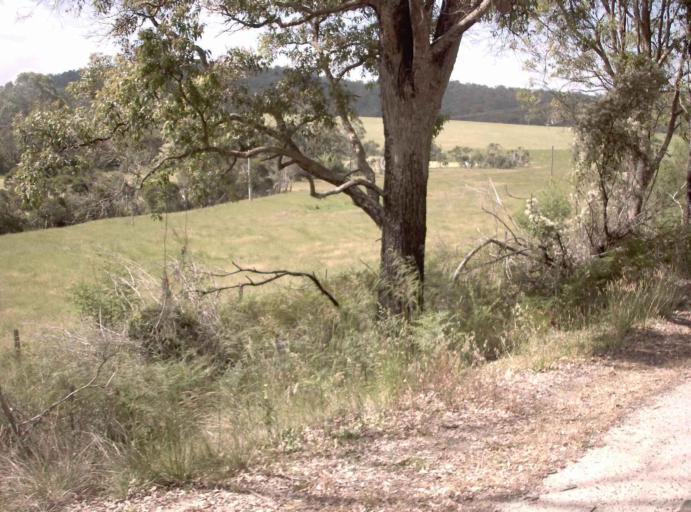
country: AU
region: New South Wales
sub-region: Bega Valley
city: Eden
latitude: -37.4806
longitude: 149.6320
